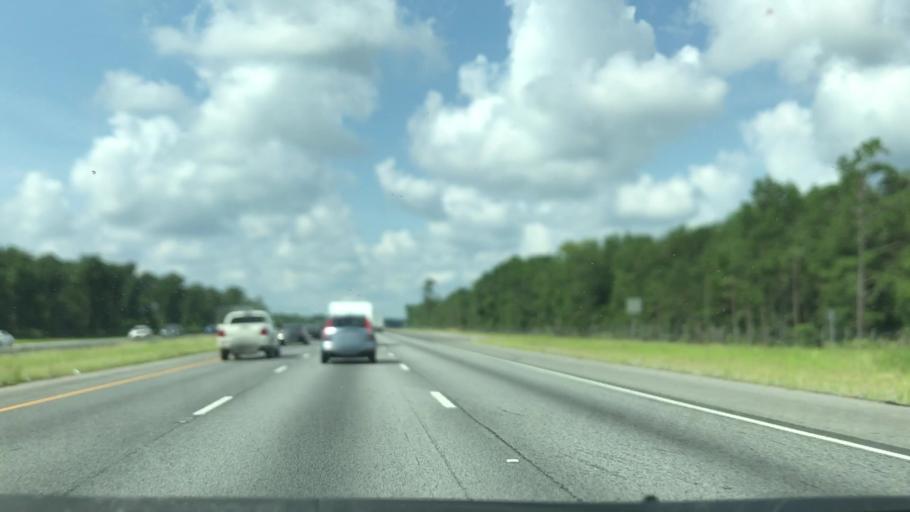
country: US
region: Georgia
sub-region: Glynn County
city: Brunswick
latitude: 31.0994
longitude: -81.6005
